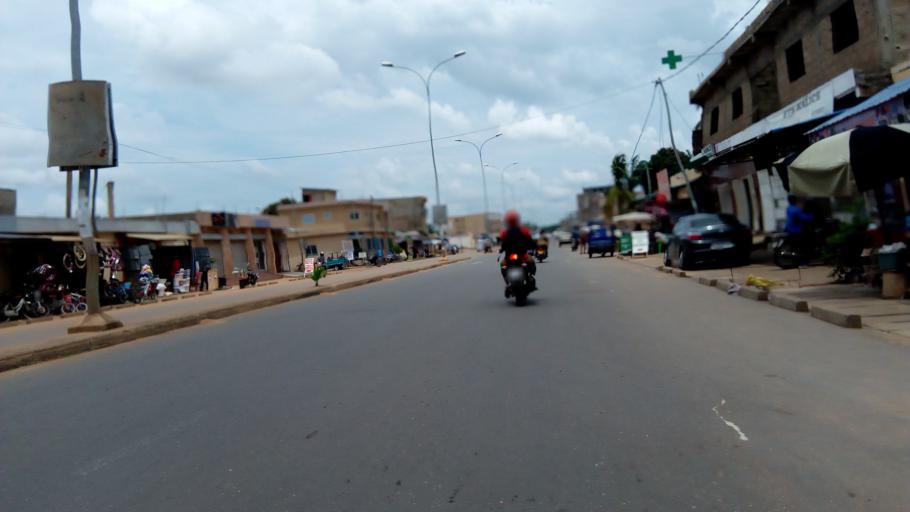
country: TG
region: Maritime
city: Lome
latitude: 6.2156
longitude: 1.1725
